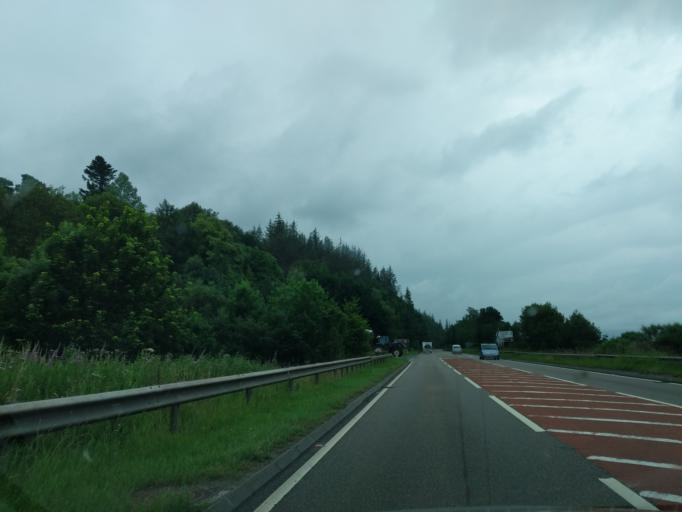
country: GB
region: Scotland
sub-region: Moray
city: Rothes
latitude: 57.4881
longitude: -3.1931
